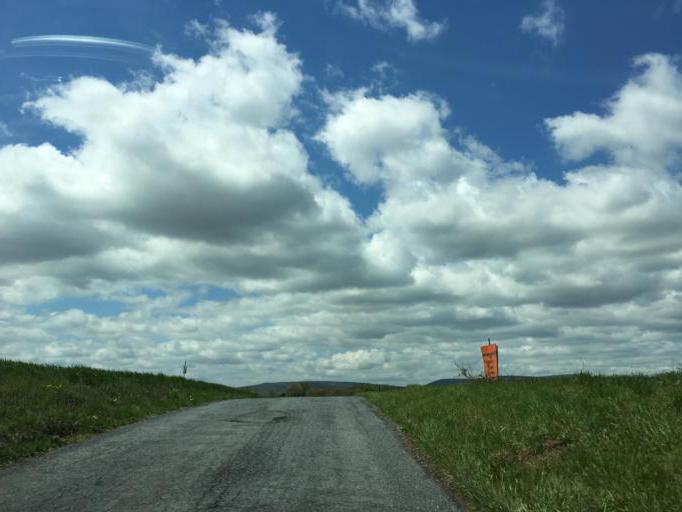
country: US
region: Maryland
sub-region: Frederick County
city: Thurmont
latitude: 39.6015
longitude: -77.3436
